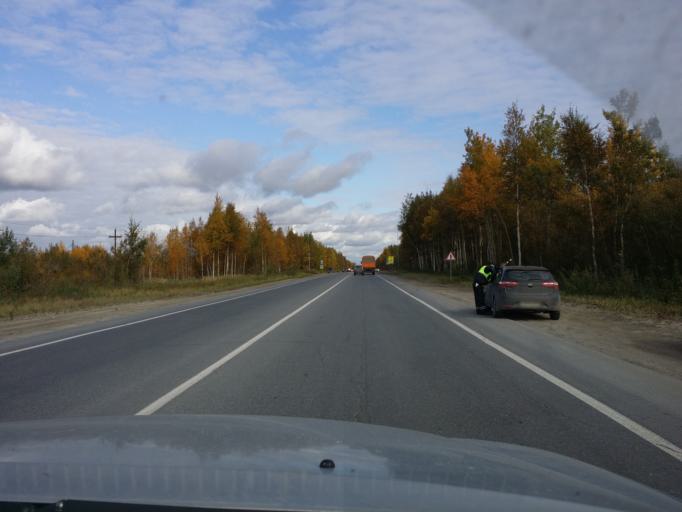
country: RU
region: Khanty-Mansiyskiy Avtonomnyy Okrug
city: Megion
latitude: 61.0618
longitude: 76.1148
